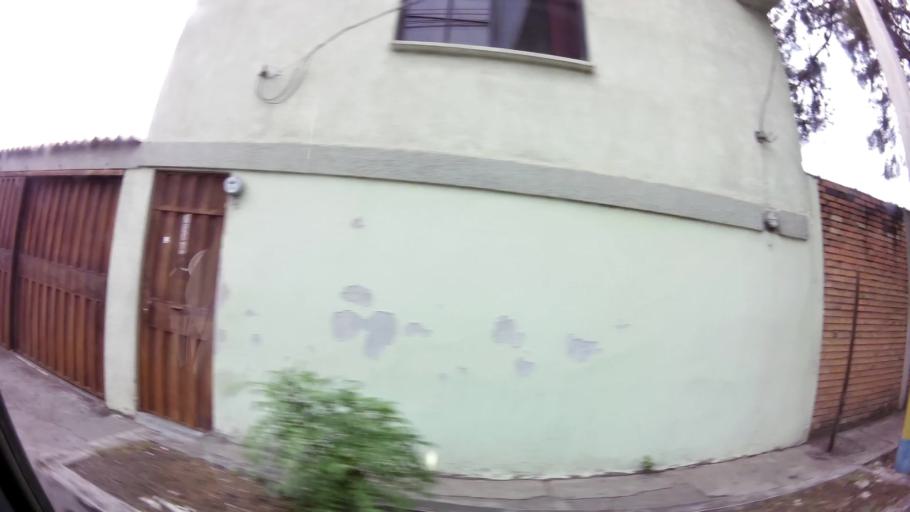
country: HN
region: Francisco Morazan
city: Tegucigalpa
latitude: 14.0845
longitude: -87.1975
